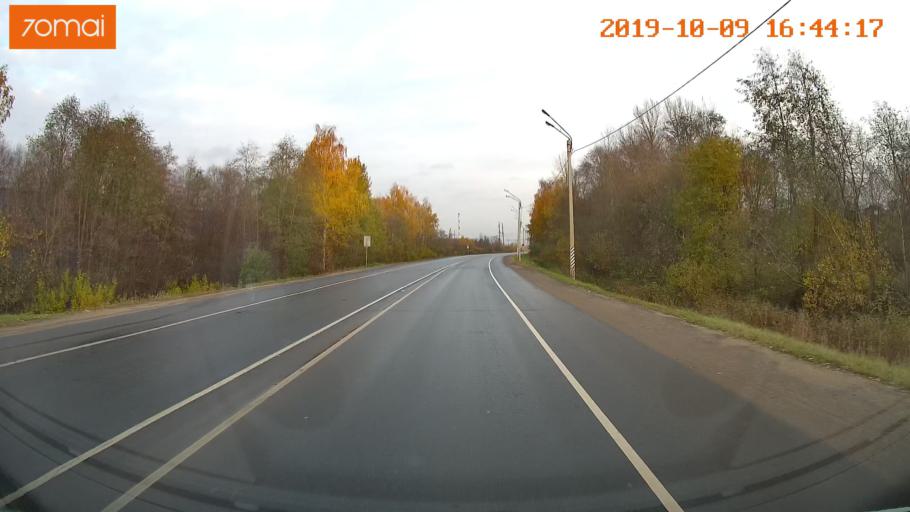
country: RU
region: Kostroma
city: Volgorechensk
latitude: 57.4520
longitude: 41.1386
